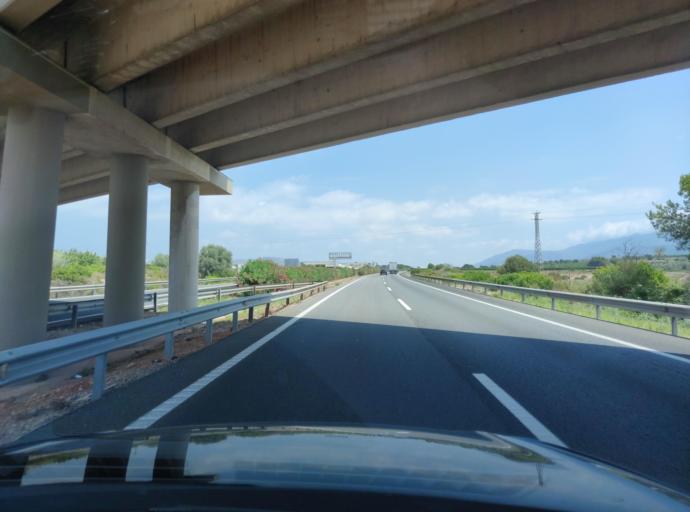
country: ES
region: Catalonia
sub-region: Provincia de Tarragona
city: Ulldecona
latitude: 40.5660
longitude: 0.4314
